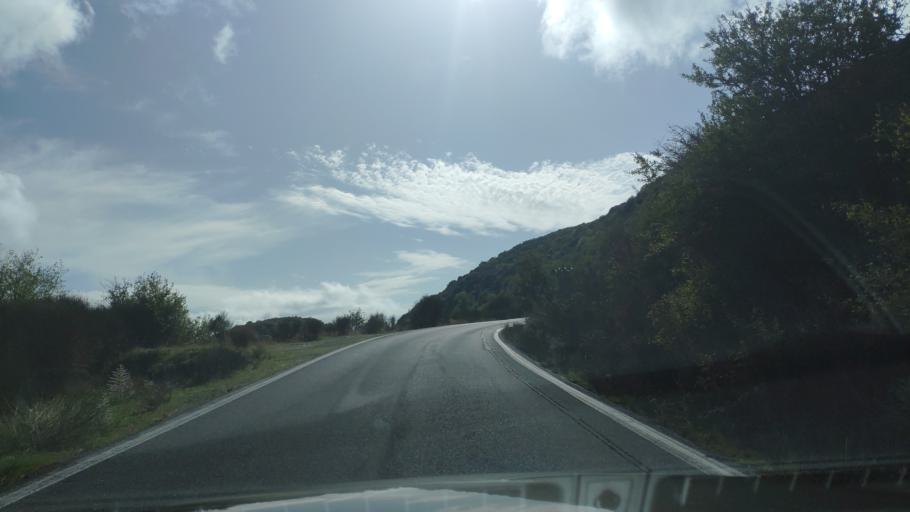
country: GR
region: Peloponnese
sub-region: Nomos Arkadias
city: Dimitsana
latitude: 37.5845
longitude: 22.0194
